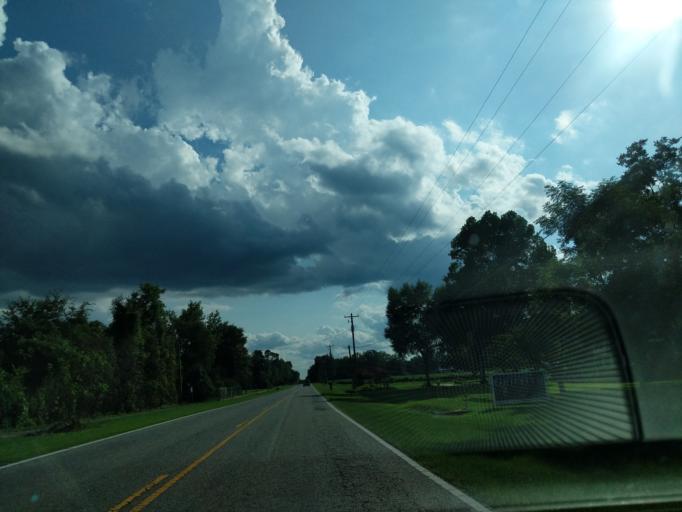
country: US
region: South Carolina
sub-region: Barnwell County
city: Williston
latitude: 33.4152
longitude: -81.4063
